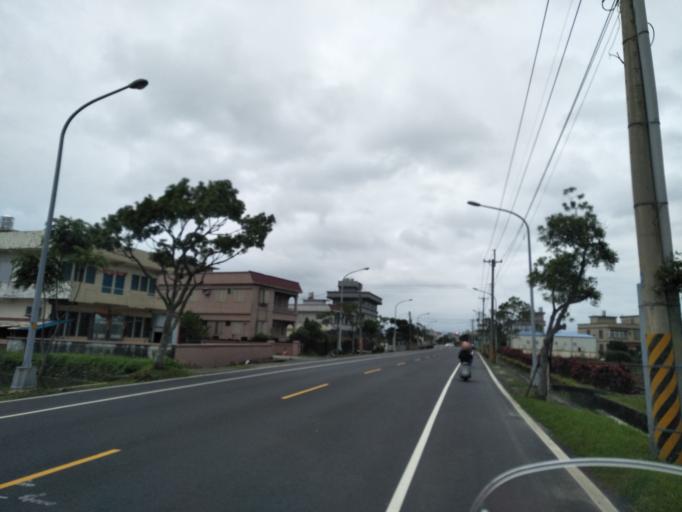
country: TW
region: Taiwan
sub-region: Yilan
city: Yilan
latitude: 24.7776
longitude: 121.7831
